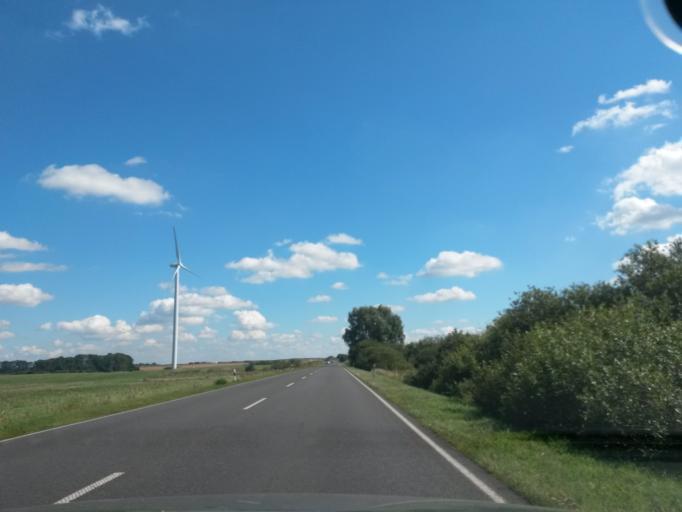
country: DE
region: Brandenburg
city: Pinnow
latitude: 53.0280
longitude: 14.0664
